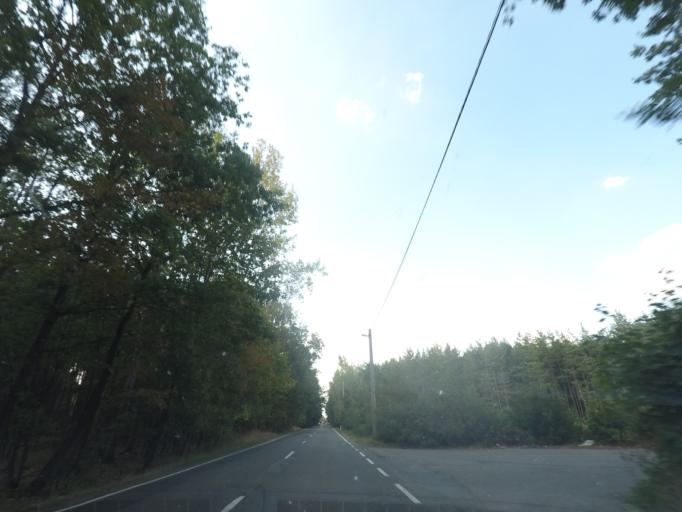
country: CZ
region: Kralovehradecky
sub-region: Okres Nachod
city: Jaromer
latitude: 50.3147
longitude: 15.9510
